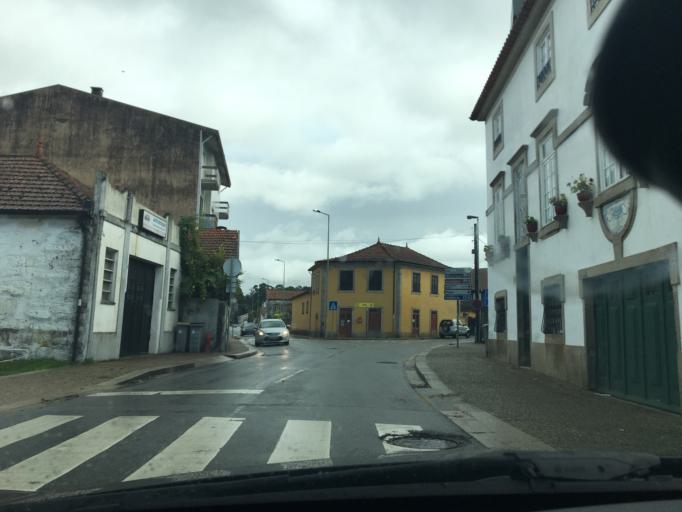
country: PT
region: Porto
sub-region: Maia
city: Gemunde
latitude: 41.2478
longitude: -8.6627
